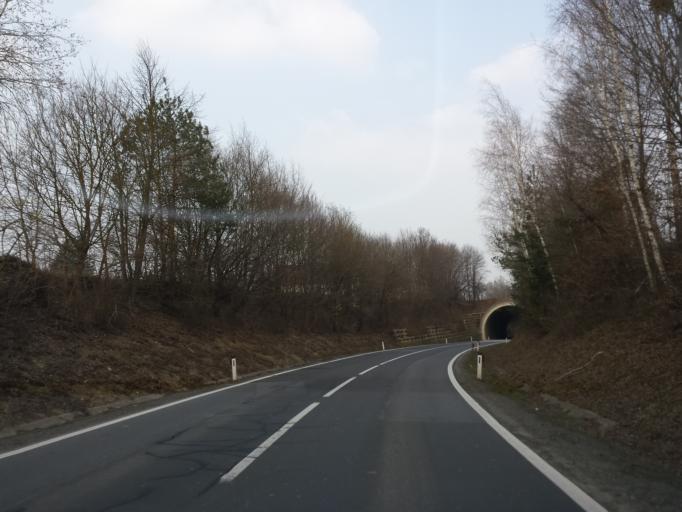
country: AT
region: Styria
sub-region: Politischer Bezirk Hartberg-Fuerstenfeld
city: Fuerstenfeld
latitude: 47.0401
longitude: 16.0966
